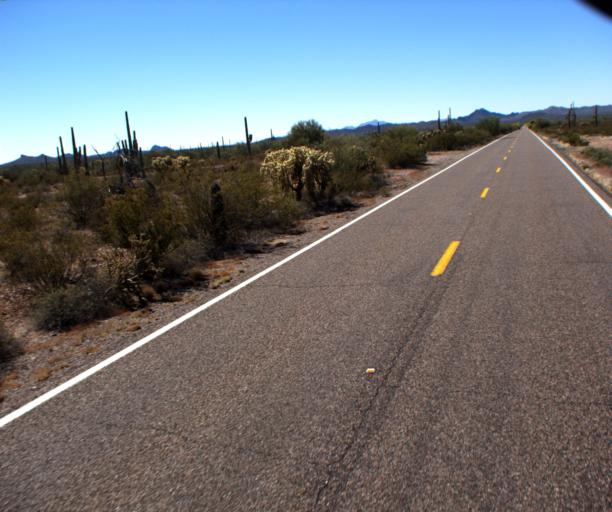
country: MX
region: Sonora
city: Sonoyta
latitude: 32.0540
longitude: -112.7899
